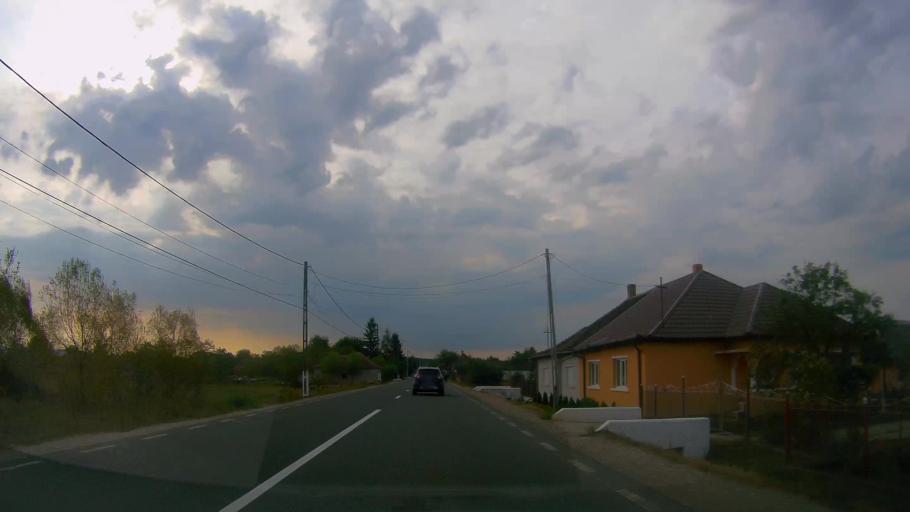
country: RO
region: Satu Mare
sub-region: Oras Ardud
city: Ardud
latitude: 47.5881
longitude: 22.8837
